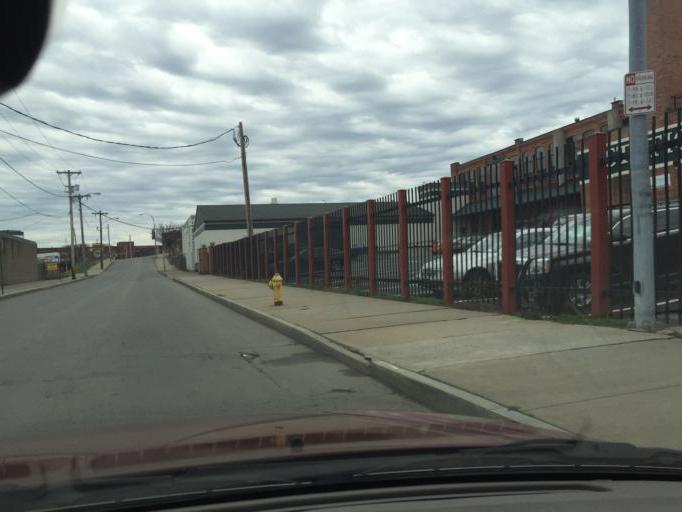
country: US
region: New York
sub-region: Monroe County
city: Rochester
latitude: 43.1631
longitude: -77.5862
